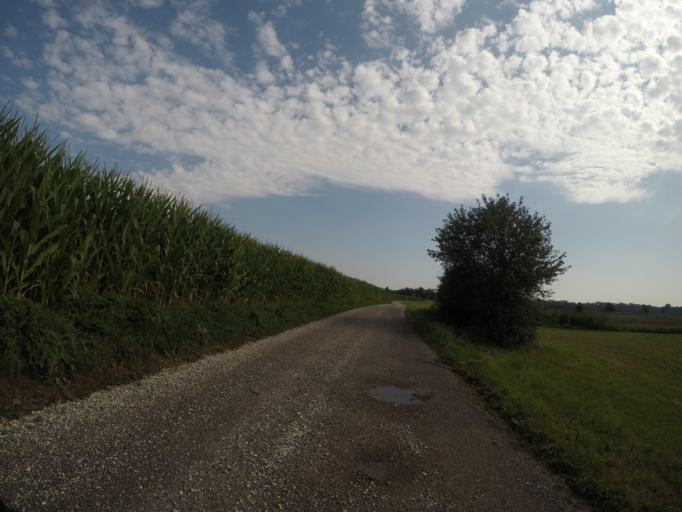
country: DE
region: Baden-Wuerttemberg
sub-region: Tuebingen Region
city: Dietenheim
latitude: 48.1923
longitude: 10.0717
